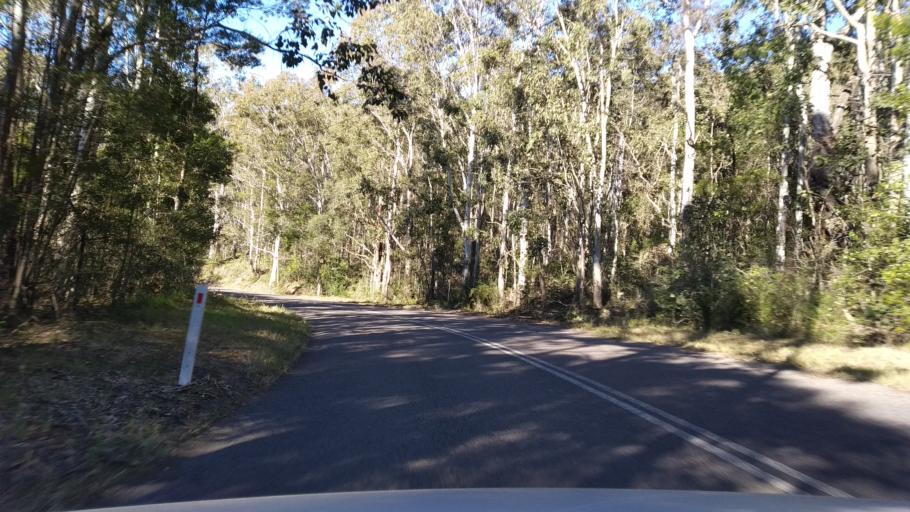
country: AU
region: New South Wales
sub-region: Wyong Shire
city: Little Jilliby
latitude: -33.2296
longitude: 151.2999
